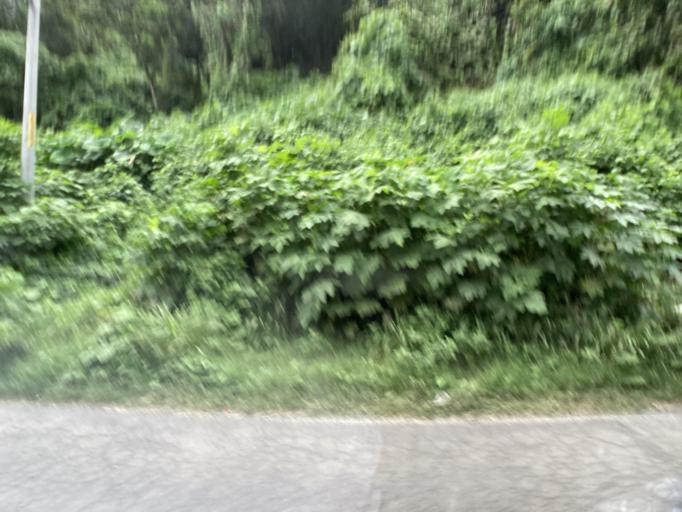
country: GT
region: Guatemala
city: Villa Canales
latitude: 14.4359
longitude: -90.5351
